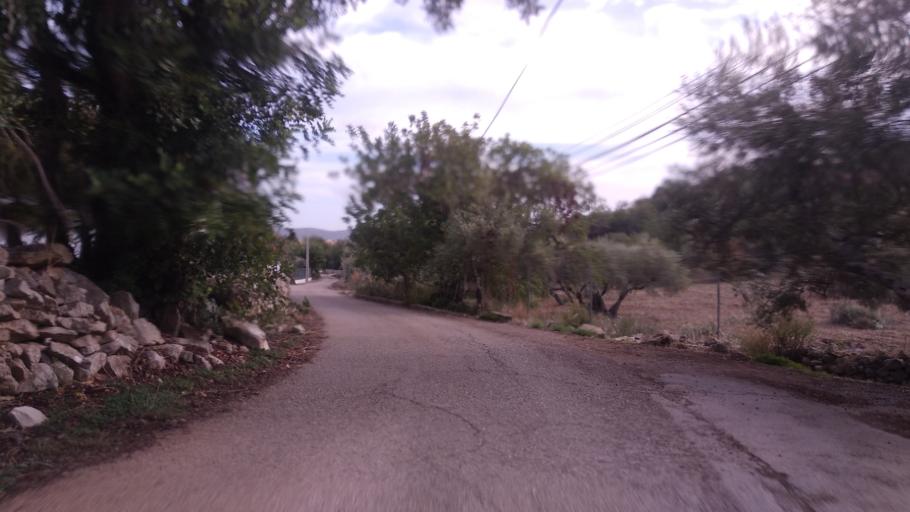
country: PT
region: Faro
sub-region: Sao Bras de Alportel
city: Sao Bras de Alportel
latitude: 37.1570
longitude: -7.8987
